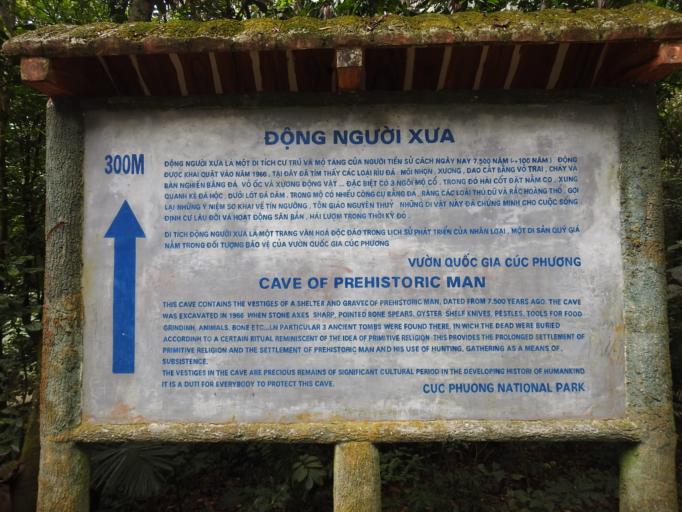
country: VN
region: Ninh Binh
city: Thi Tran Nho Quan
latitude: 20.2928
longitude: 105.6670
